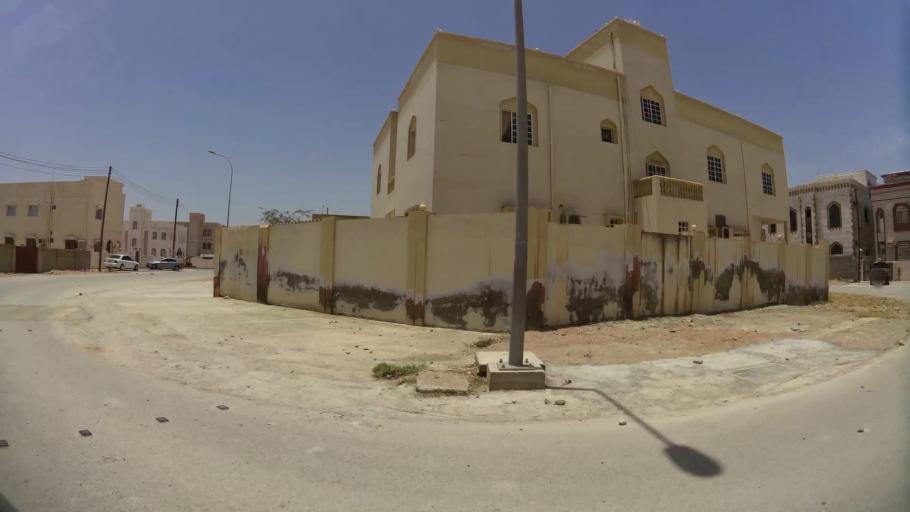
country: OM
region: Zufar
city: Salalah
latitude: 17.0745
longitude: 54.1576
